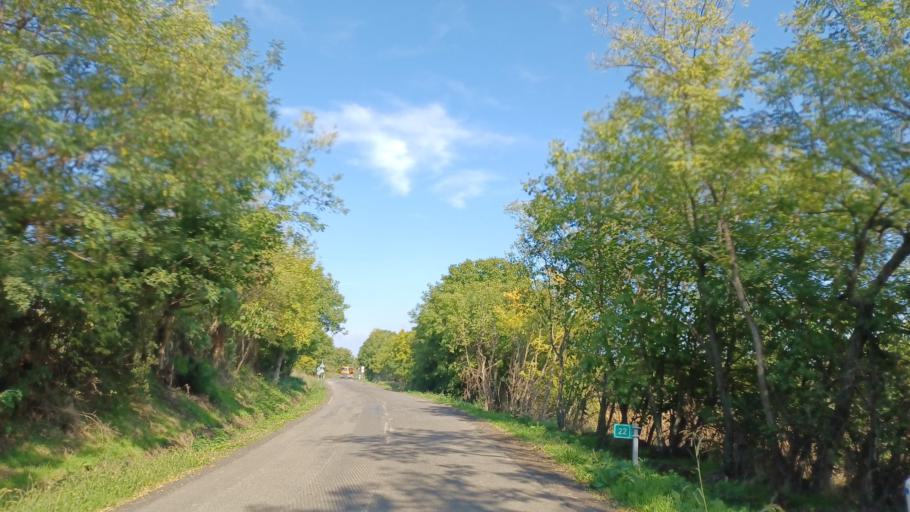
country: HU
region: Tolna
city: Nagydorog
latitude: 46.5914
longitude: 18.5963
